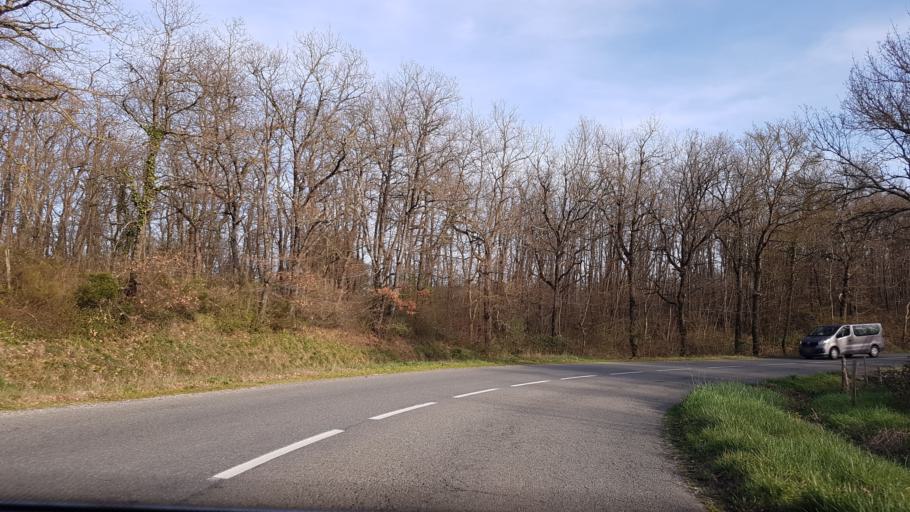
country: FR
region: Languedoc-Roussillon
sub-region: Departement de l'Aude
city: Villeneuve-la-Comptal
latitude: 43.2369
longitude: 1.9199
